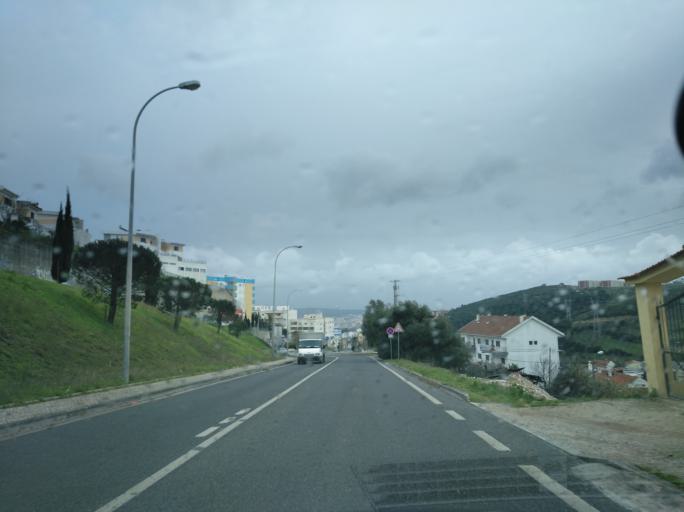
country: PT
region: Lisbon
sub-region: Odivelas
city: Famoes
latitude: 38.7931
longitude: -9.2288
